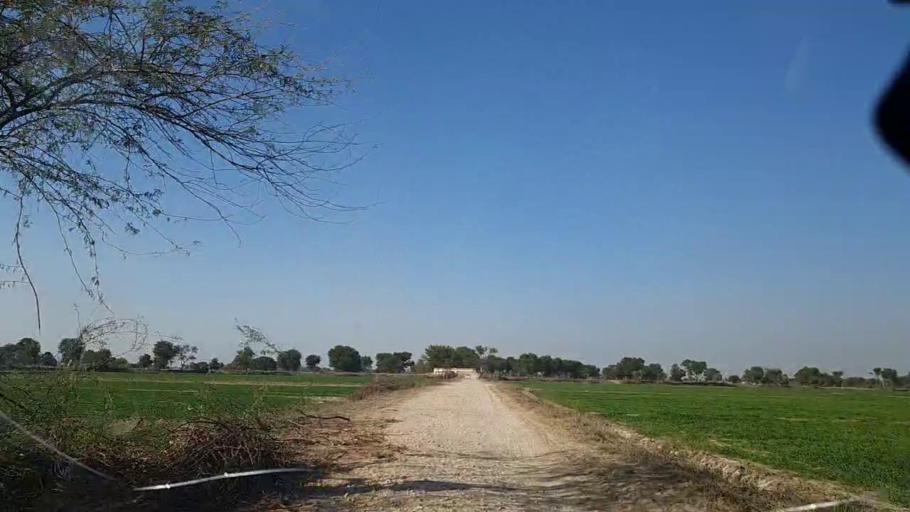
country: PK
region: Sindh
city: Khanpur
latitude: 27.7875
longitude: 69.3520
